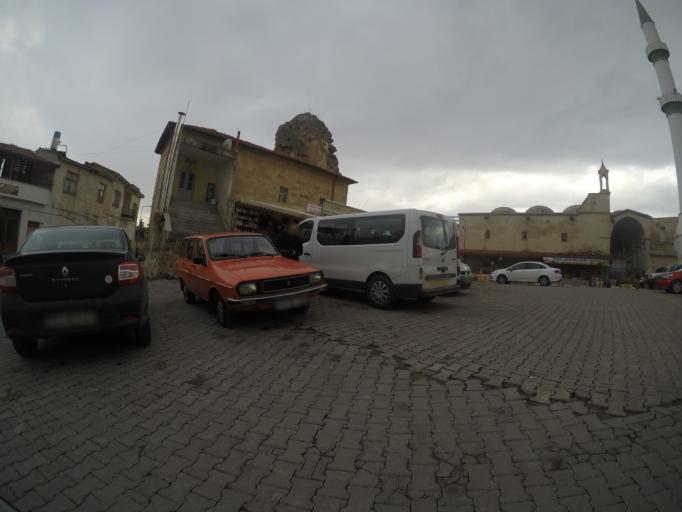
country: TR
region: Nevsehir
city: Goereme
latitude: 38.6207
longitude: 34.8651
